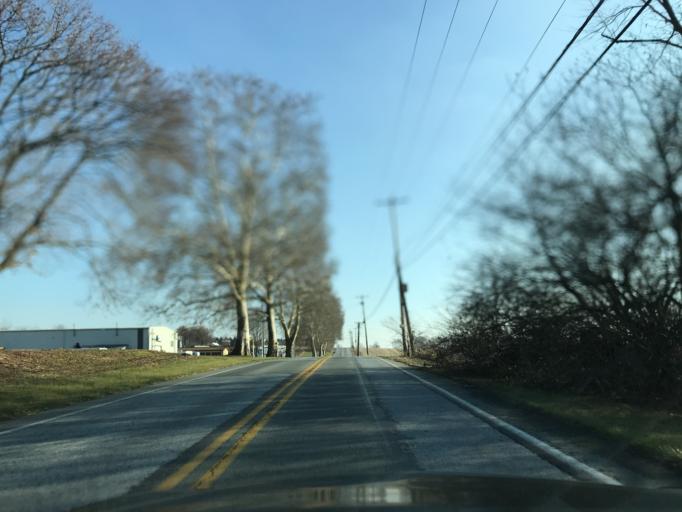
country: US
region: Pennsylvania
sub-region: York County
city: Loganville
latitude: 39.8155
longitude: -76.6883
